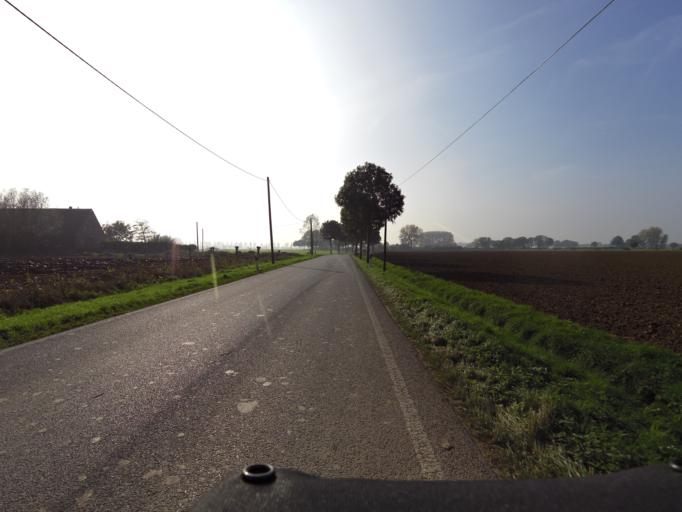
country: DE
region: North Rhine-Westphalia
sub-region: Regierungsbezirk Dusseldorf
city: Kranenburg
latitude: 51.8451
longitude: 6.0388
